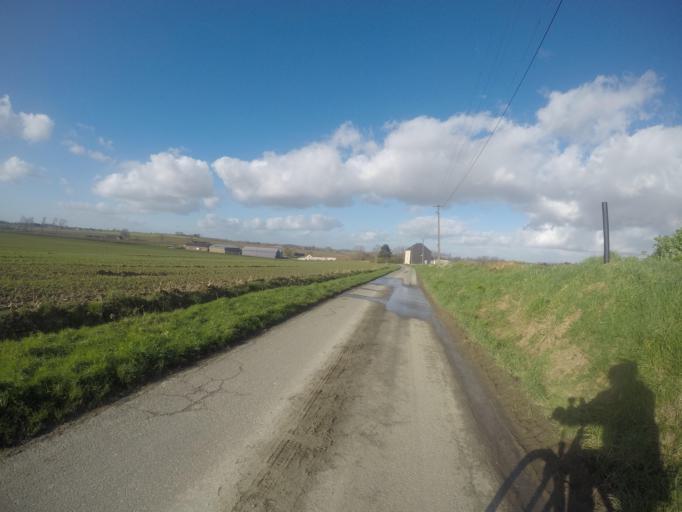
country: BE
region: Wallonia
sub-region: Province du Brabant Wallon
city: Rebecq-Rognon
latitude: 50.6870
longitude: 4.1461
